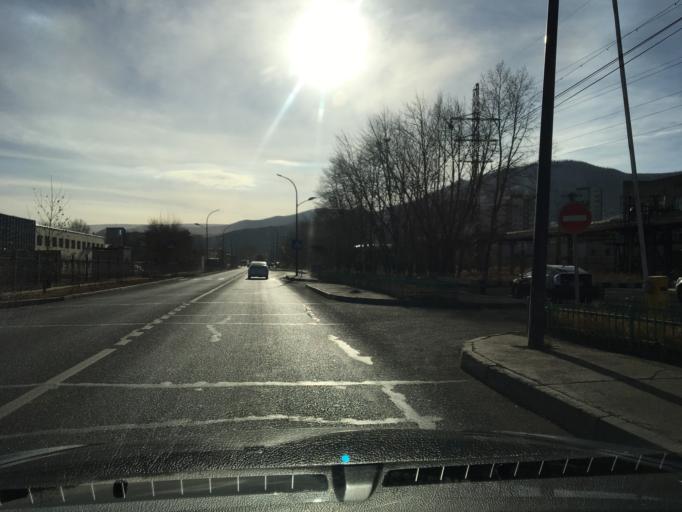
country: MN
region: Ulaanbaatar
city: Ulaanbaatar
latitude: 47.8955
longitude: 106.8733
